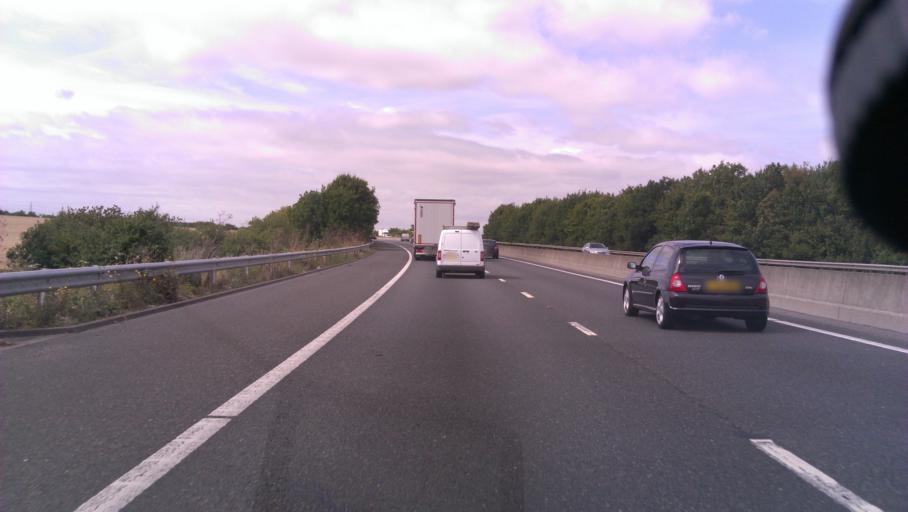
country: GB
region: England
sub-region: Essex
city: Elsenham
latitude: 51.9713
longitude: 0.2128
